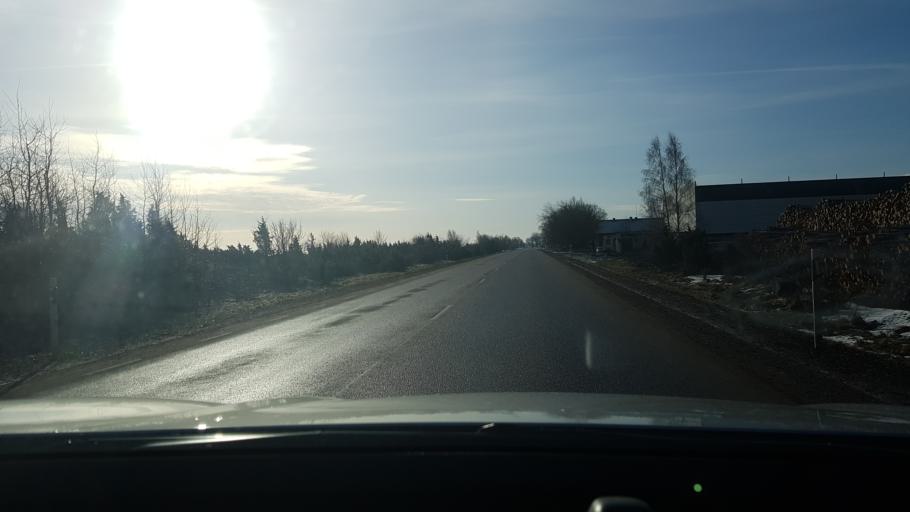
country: EE
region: Saare
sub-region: Kuressaare linn
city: Kuressaare
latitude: 58.2279
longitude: 22.5054
